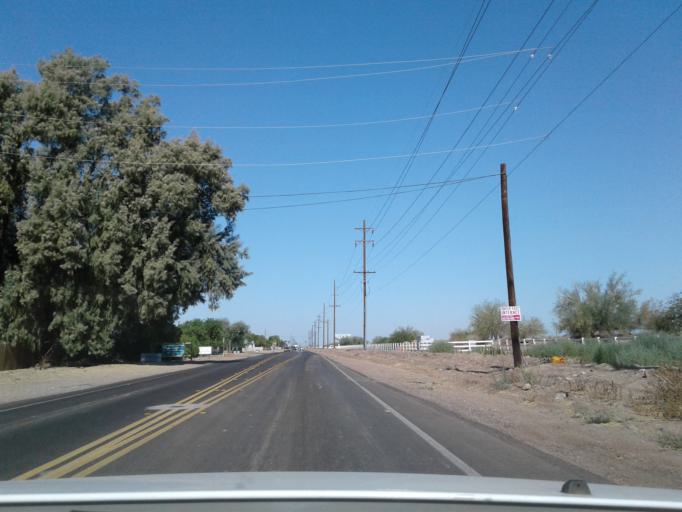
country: US
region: Arizona
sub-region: Maricopa County
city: Laveen
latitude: 33.3919
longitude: -112.1941
